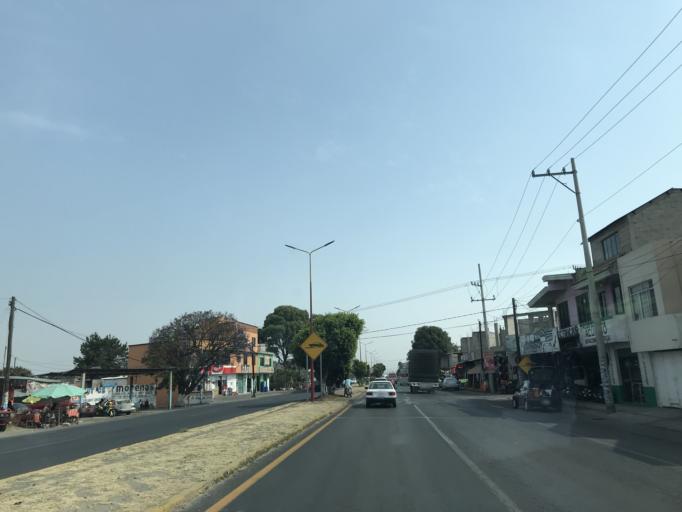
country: MX
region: Tlaxcala
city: La Magdalena Tlaltelulco
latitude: 19.2798
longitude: -98.1962
